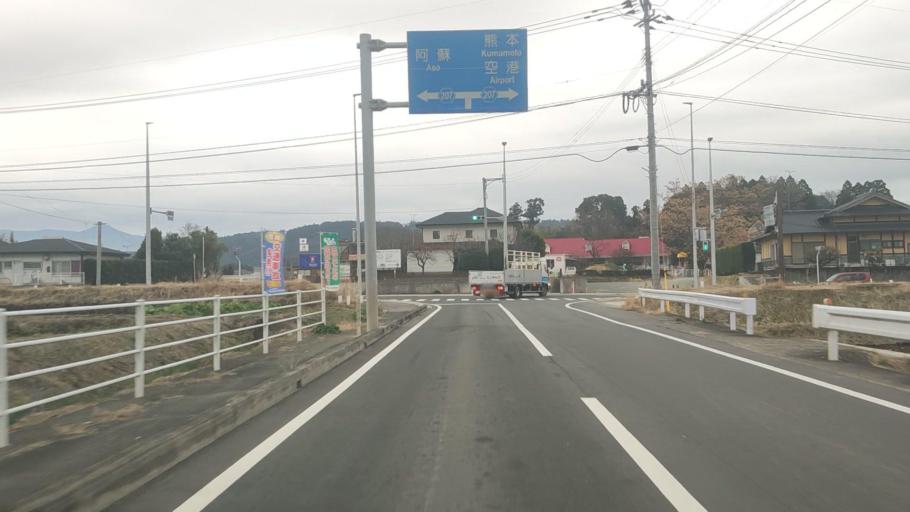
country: JP
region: Kumamoto
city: Ozu
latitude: 32.8656
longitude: 130.8907
